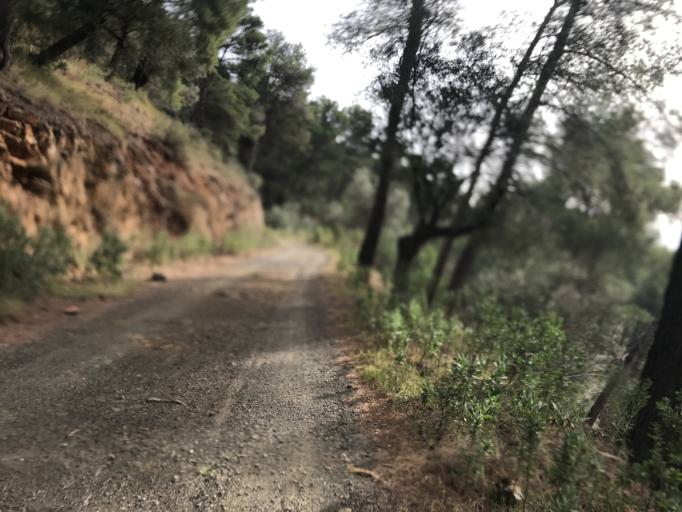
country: ES
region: Andalusia
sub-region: Provincia de Malaga
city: Malaga
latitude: 36.8034
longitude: -4.3997
